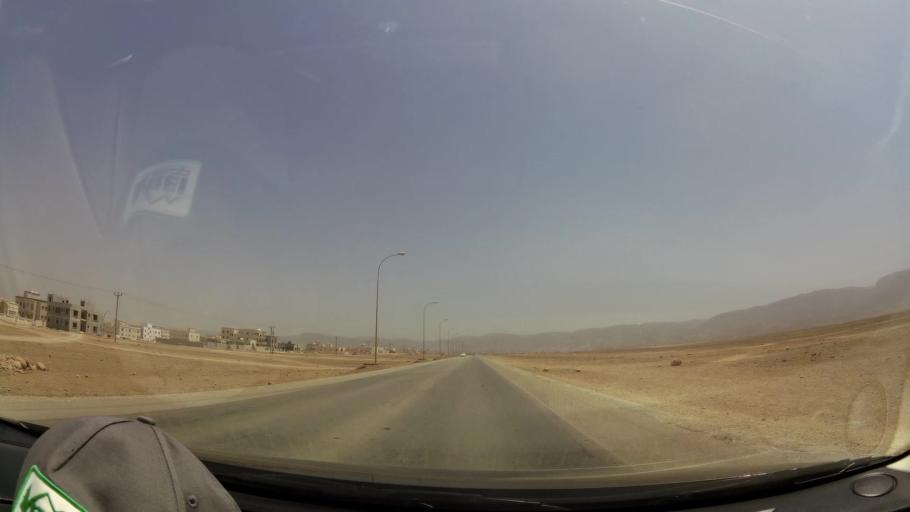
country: OM
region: Zufar
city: Salalah
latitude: 17.0754
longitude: 54.2171
